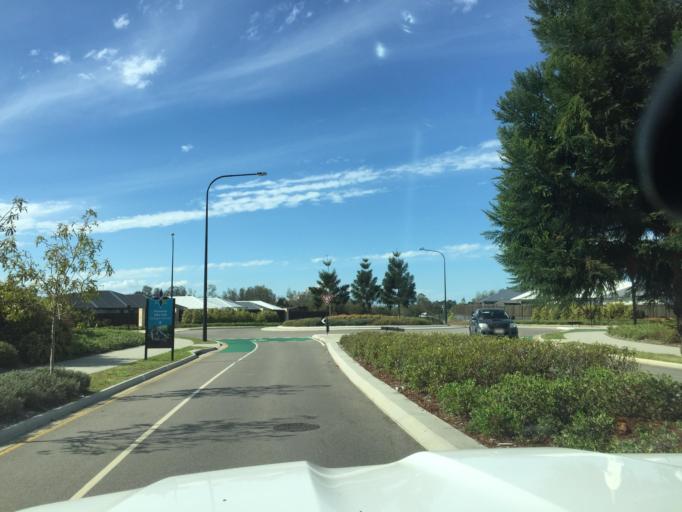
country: AU
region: Queensland
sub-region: Moreton Bay
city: Morayfield
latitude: -27.1186
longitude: 152.9935
